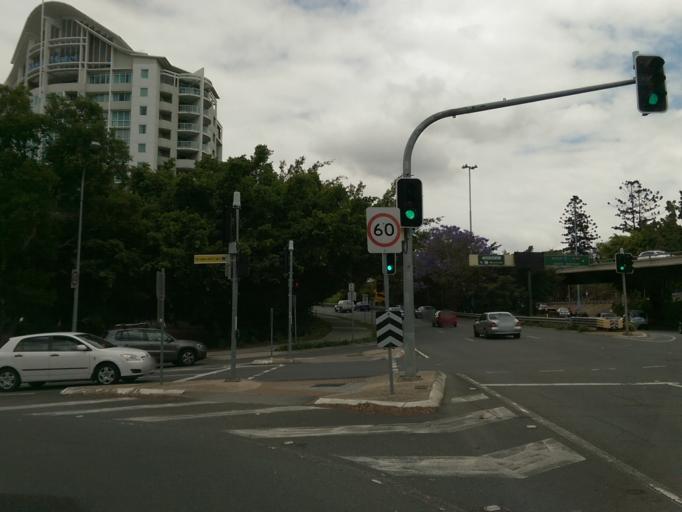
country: AU
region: Queensland
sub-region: Brisbane
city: Brisbane
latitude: -27.4731
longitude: 153.0360
